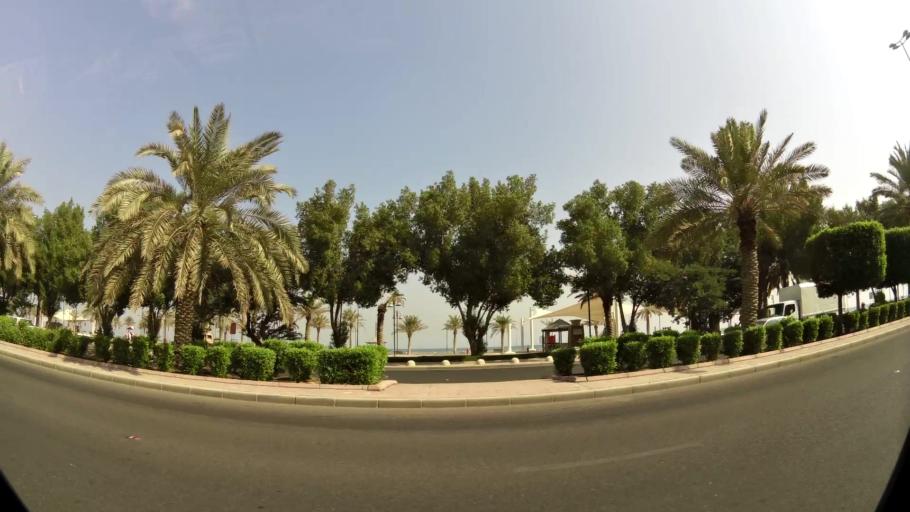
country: KW
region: Al Ahmadi
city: Al Fintas
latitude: 29.1775
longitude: 48.1218
